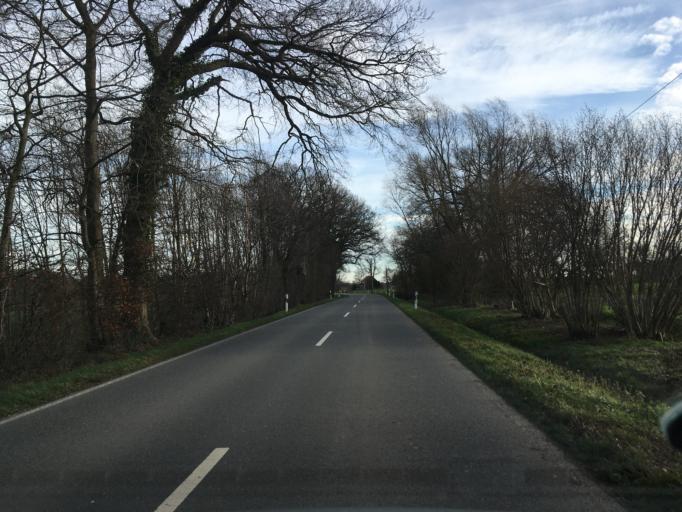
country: DE
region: North Rhine-Westphalia
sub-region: Regierungsbezirk Munster
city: Schoppingen
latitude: 52.0506
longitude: 7.1978
